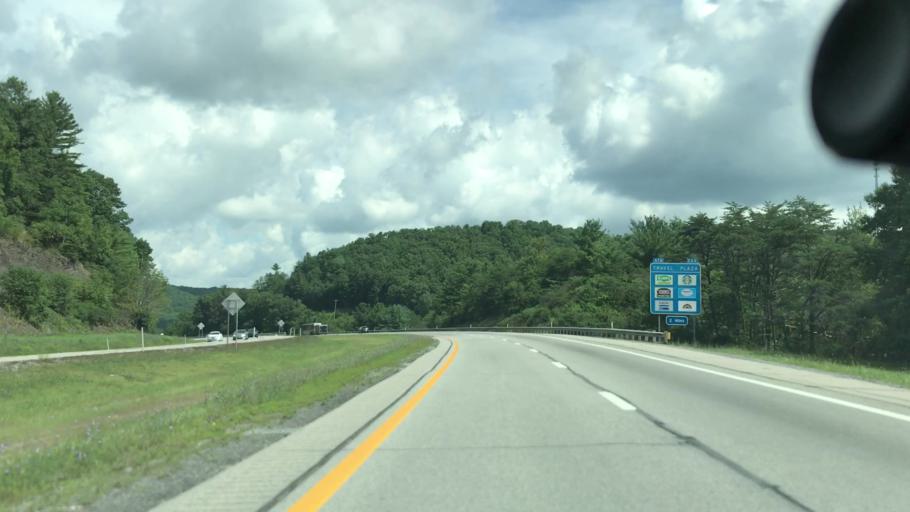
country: US
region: West Virginia
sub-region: Mercer County
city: Athens
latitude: 37.4393
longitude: -81.0643
